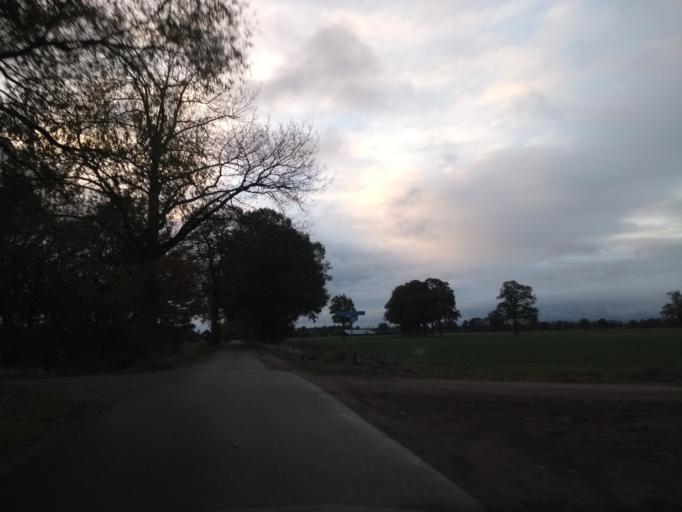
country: NL
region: Gelderland
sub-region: Gemeente Bronckhorst
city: Zelhem
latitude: 52.0191
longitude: 6.3726
